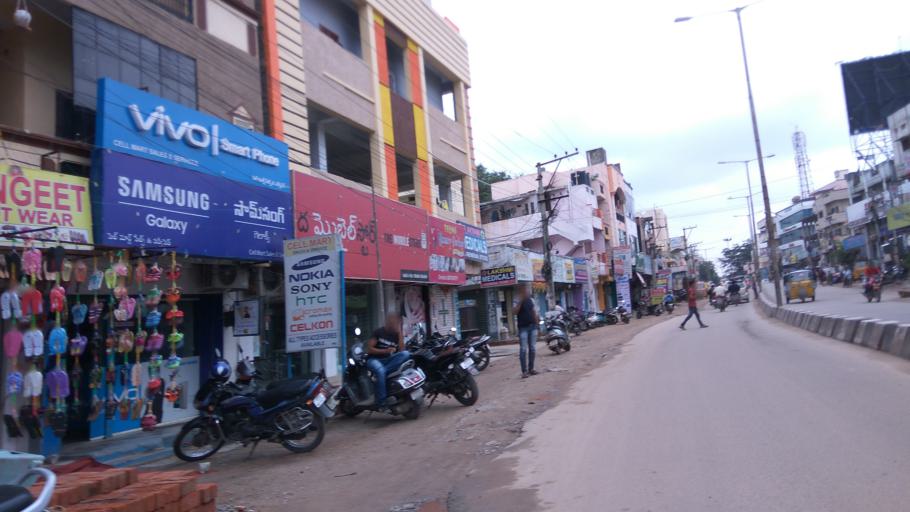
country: IN
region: Telangana
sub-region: Hyderabad
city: Malkajgiri
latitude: 17.4536
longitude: 78.5344
